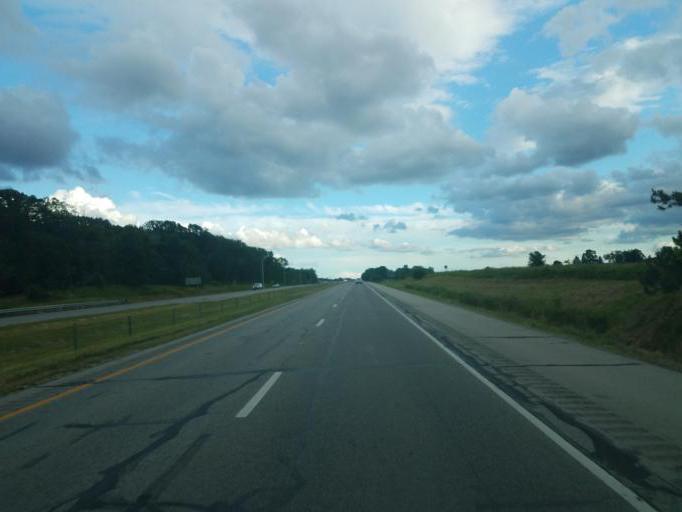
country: US
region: Indiana
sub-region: DeKalb County
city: Garrett
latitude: 41.3066
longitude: -85.0878
